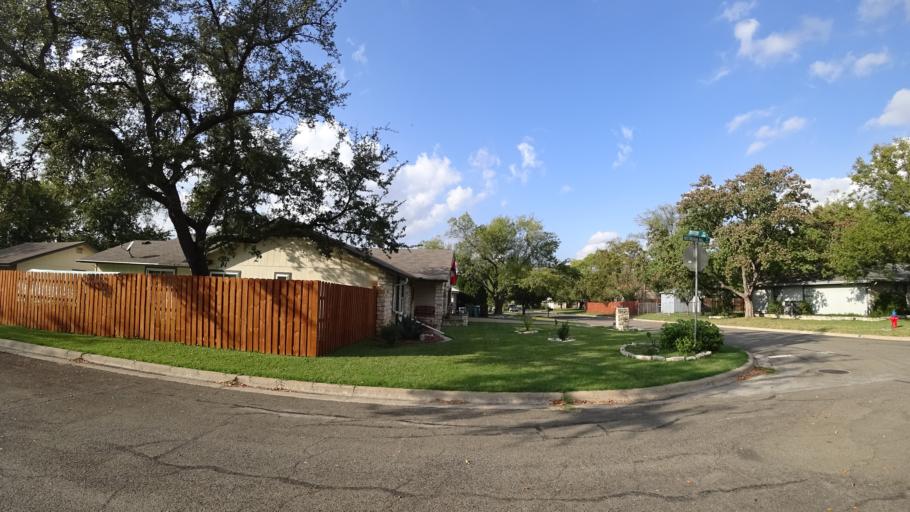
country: US
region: Texas
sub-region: Williamson County
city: Round Rock
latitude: 30.4878
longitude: -97.6663
